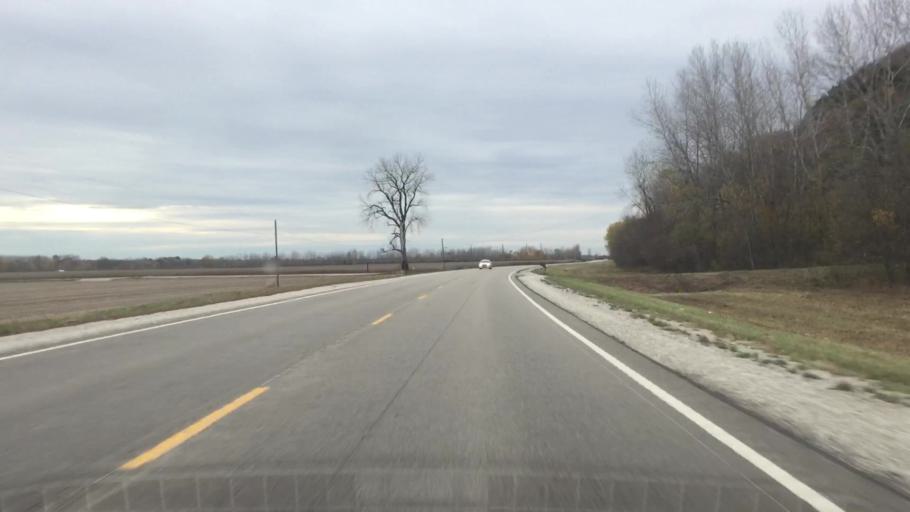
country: US
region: Missouri
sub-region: Callaway County
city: Holts Summit
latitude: 38.5805
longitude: -92.0977
